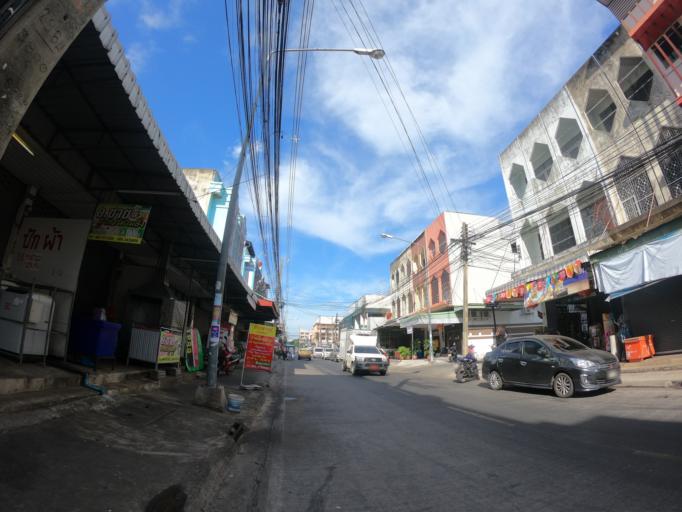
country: TH
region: Khon Kaen
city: Khon Kaen
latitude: 16.4369
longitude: 102.8328
